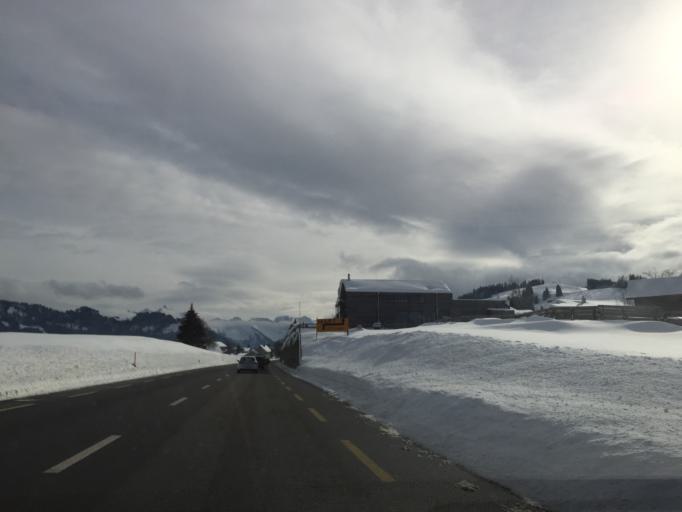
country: CH
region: Schwyz
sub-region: Bezirk Einsiedeln
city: Einsiedeln
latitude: 47.1368
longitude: 8.7607
